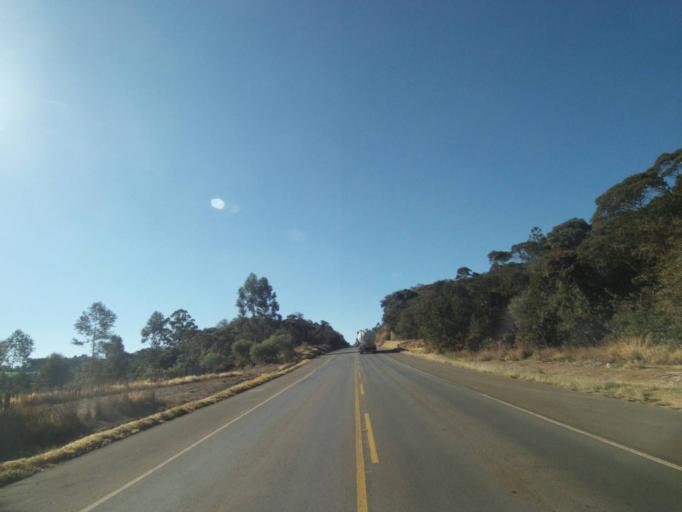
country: BR
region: Parana
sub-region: Tibagi
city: Tibagi
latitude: -24.6086
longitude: -50.4426
